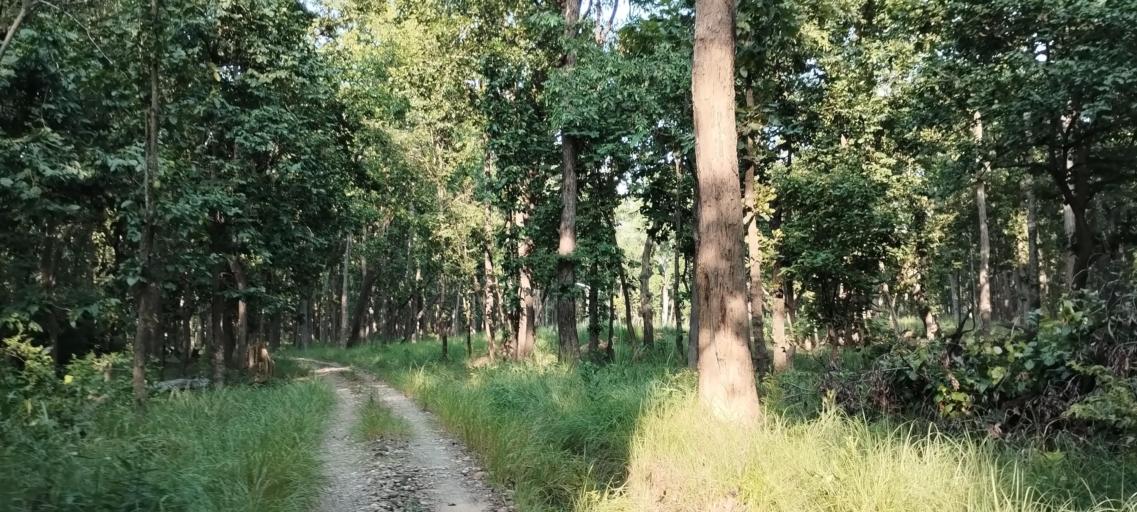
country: NP
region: Far Western
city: Tikapur
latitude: 28.5189
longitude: 81.2819
